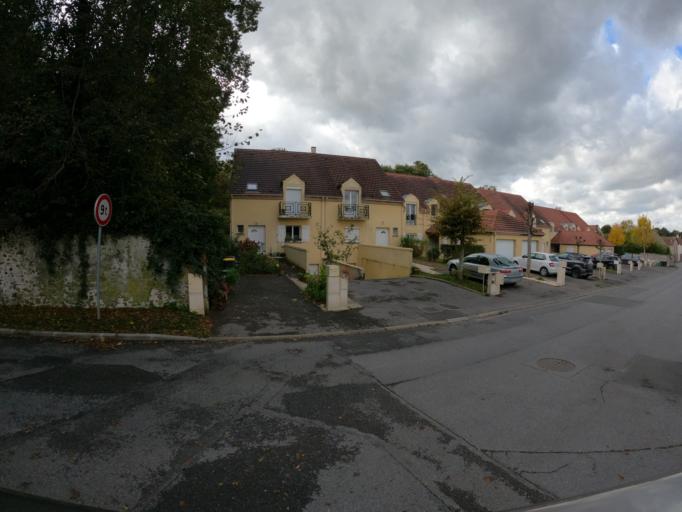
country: FR
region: Ile-de-France
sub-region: Departement de Seine-et-Marne
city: Chalifert
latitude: 48.9081
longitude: 2.7815
